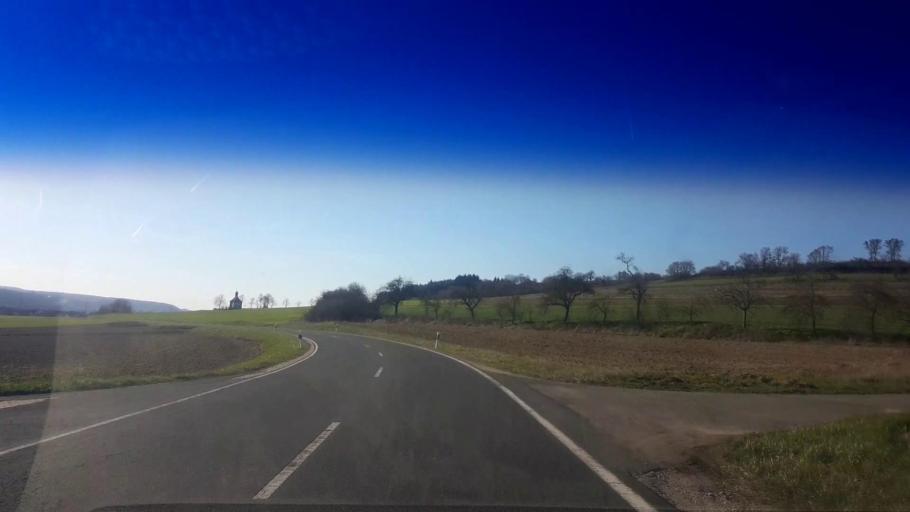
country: DE
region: Bavaria
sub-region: Regierungsbezirk Unterfranken
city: Stettfeld
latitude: 49.9680
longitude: 10.7429
